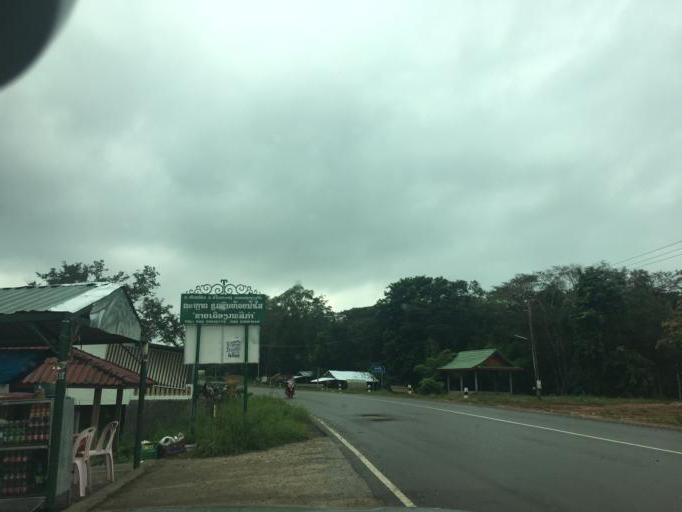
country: TH
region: Nong Khai
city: Pho Tak
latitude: 17.9869
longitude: 102.4371
